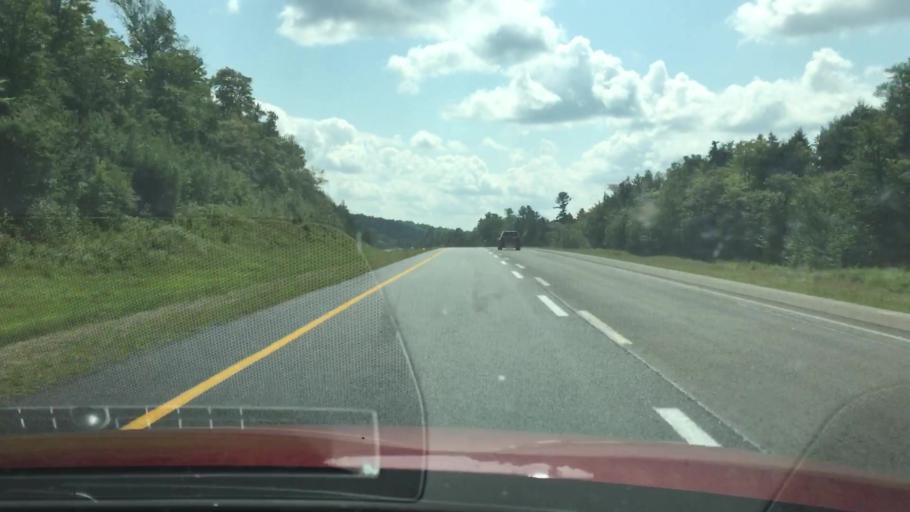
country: US
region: Maine
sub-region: Penobscot County
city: Medway
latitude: 45.7218
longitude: -68.4749
